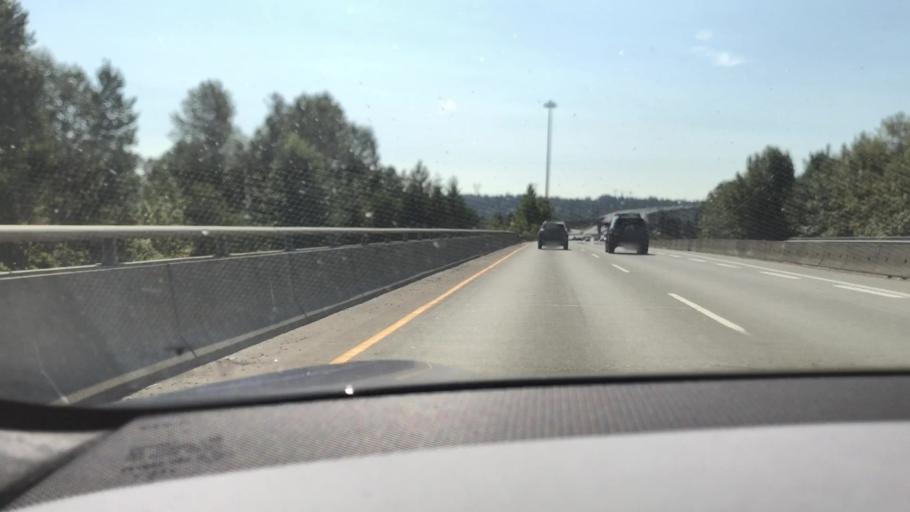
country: CA
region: British Columbia
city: New Westminster
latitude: 49.1741
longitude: -122.9574
